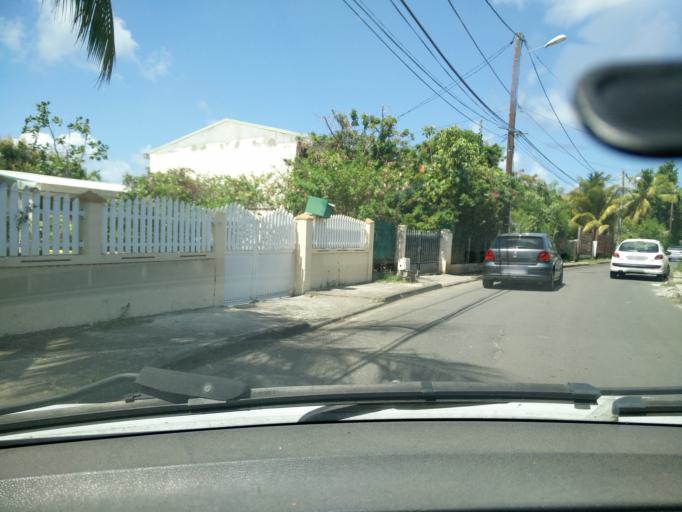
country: GP
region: Guadeloupe
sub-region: Guadeloupe
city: Le Moule
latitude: 16.3309
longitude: -61.3402
